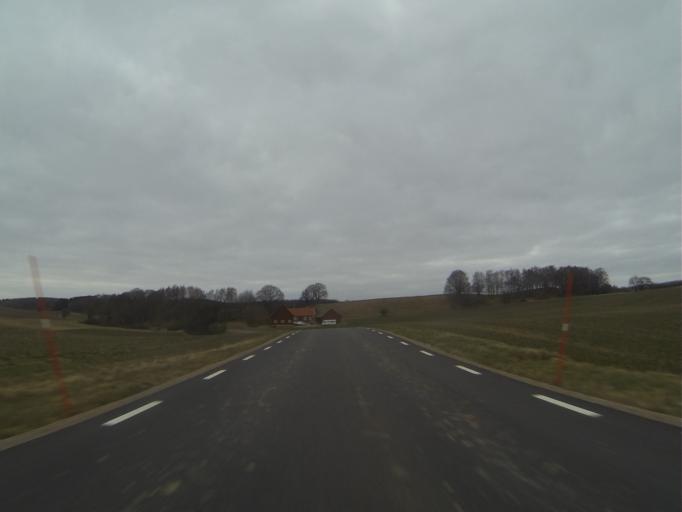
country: SE
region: Skane
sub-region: Lunds Kommun
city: Genarp
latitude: 55.5453
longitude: 13.4466
